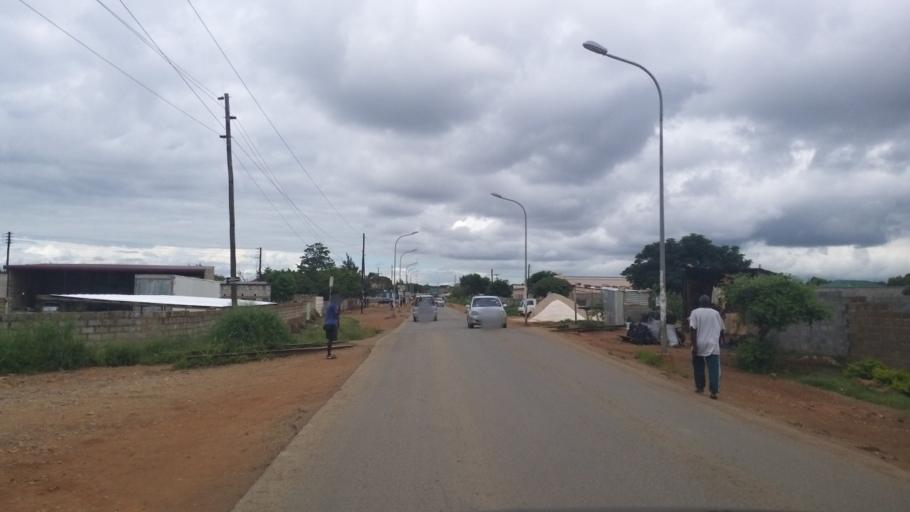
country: ZM
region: Lusaka
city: Lusaka
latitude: -15.4438
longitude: 28.3071
